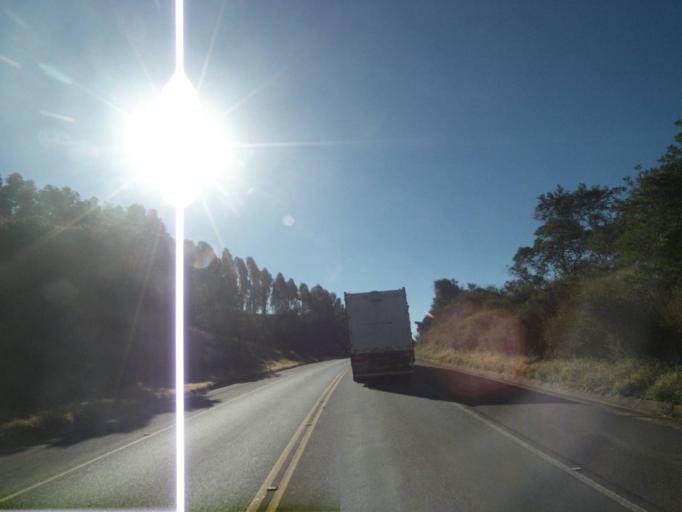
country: BR
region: Parana
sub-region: Tibagi
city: Tibagi
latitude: -24.5639
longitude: -50.4544
